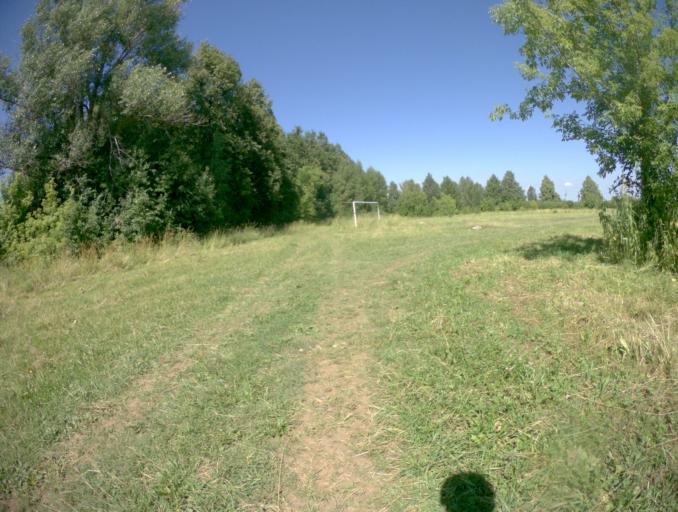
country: RU
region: Nizjnij Novgorod
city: Gorbatov
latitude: 56.1320
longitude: 43.0424
